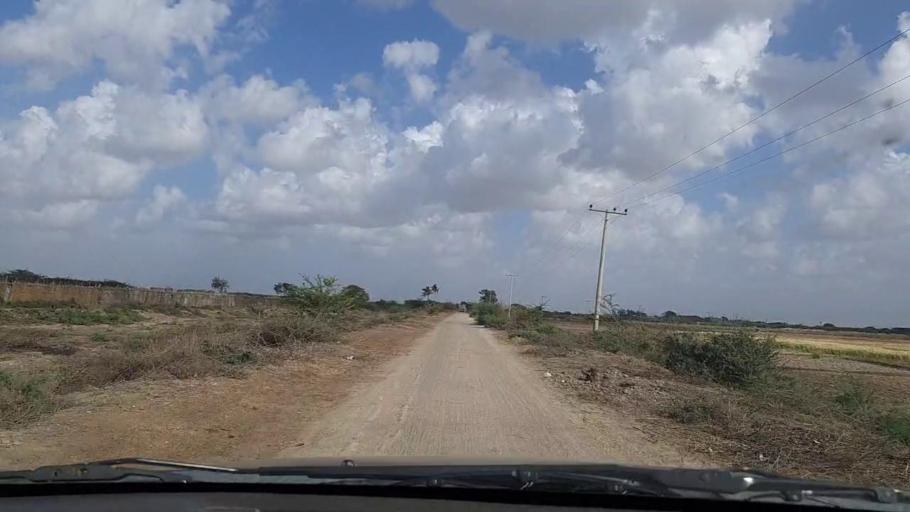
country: PK
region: Sindh
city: Keti Bandar
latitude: 24.0957
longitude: 67.6090
